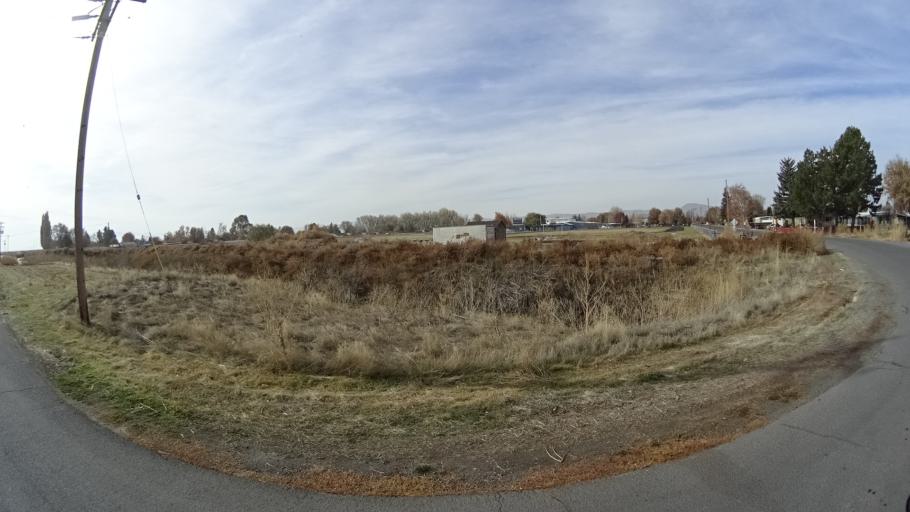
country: US
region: California
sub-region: Siskiyou County
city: Tulelake
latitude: 41.9508
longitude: -121.4716
